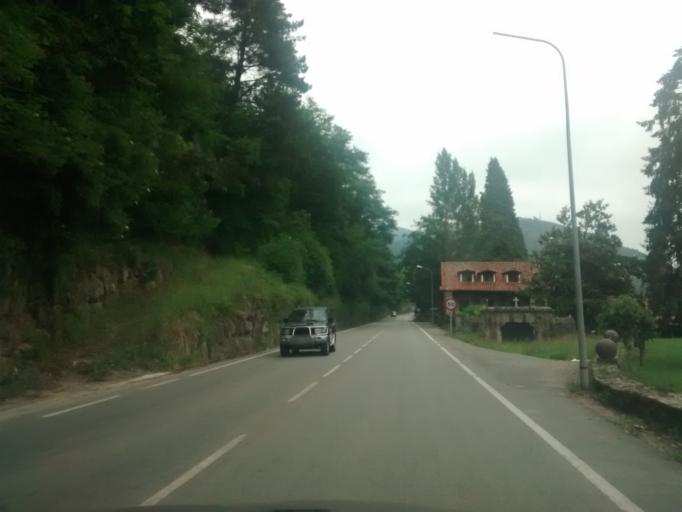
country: ES
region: Cantabria
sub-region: Provincia de Cantabria
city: Ruente
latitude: 43.2235
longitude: -4.3022
